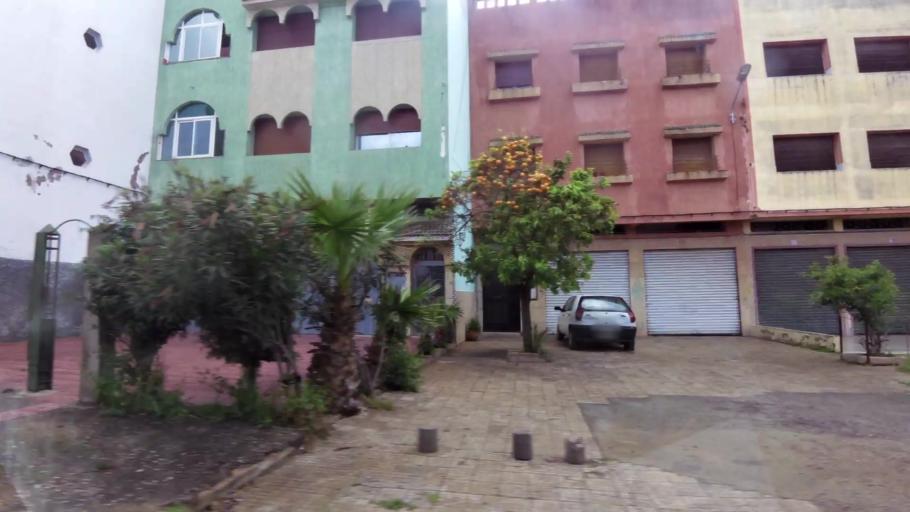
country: MA
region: Grand Casablanca
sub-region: Casablanca
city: Casablanca
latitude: 33.5596
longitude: -7.6832
